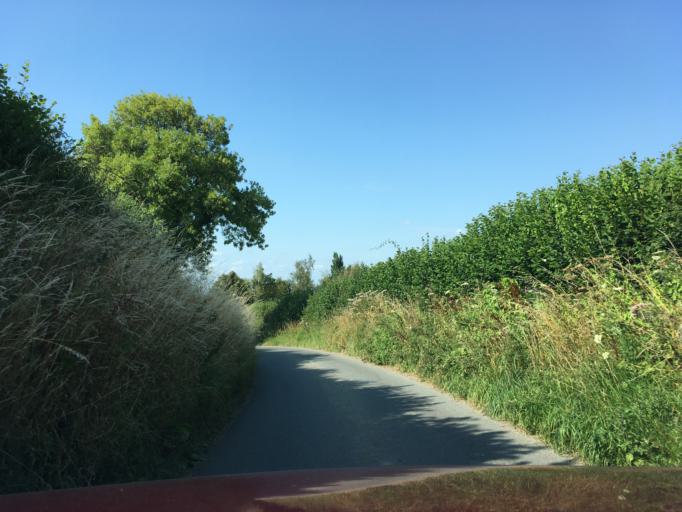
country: GB
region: England
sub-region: Gloucestershire
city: Dursley
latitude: 51.6990
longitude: -2.3158
